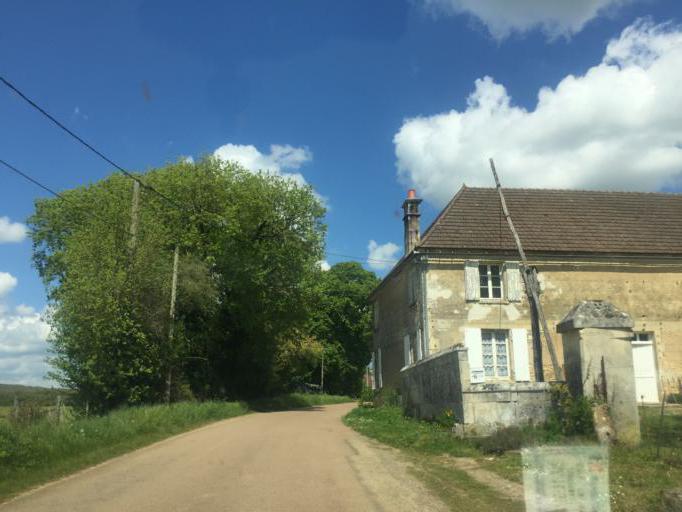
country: FR
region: Bourgogne
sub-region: Departement de l'Yonne
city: Fontenailles
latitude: 47.5264
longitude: 3.3475
